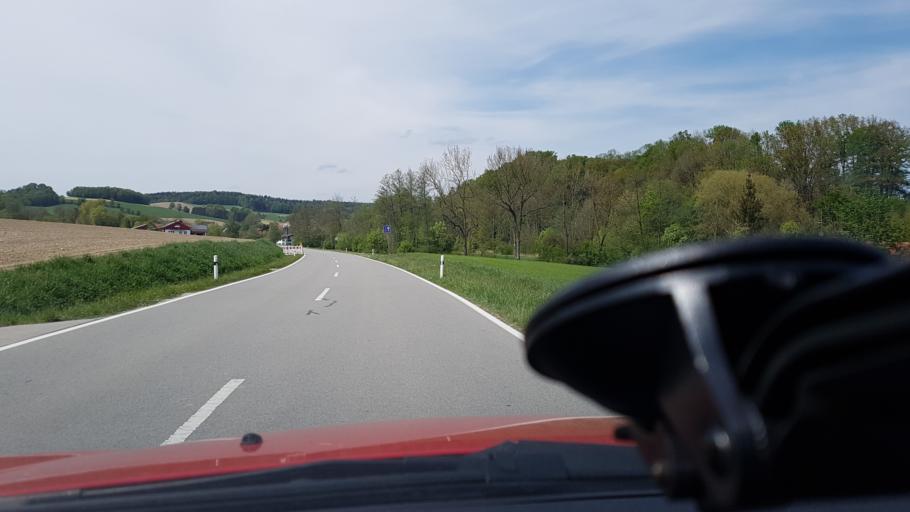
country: DE
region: Bavaria
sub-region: Lower Bavaria
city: Ering
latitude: 48.3215
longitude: 13.1339
